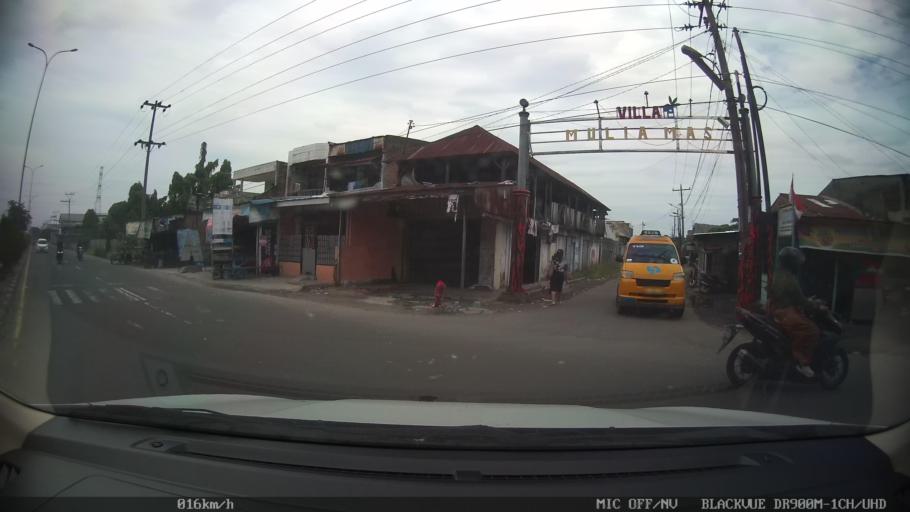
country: ID
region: North Sumatra
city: Sunggal
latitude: 3.6011
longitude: 98.5902
